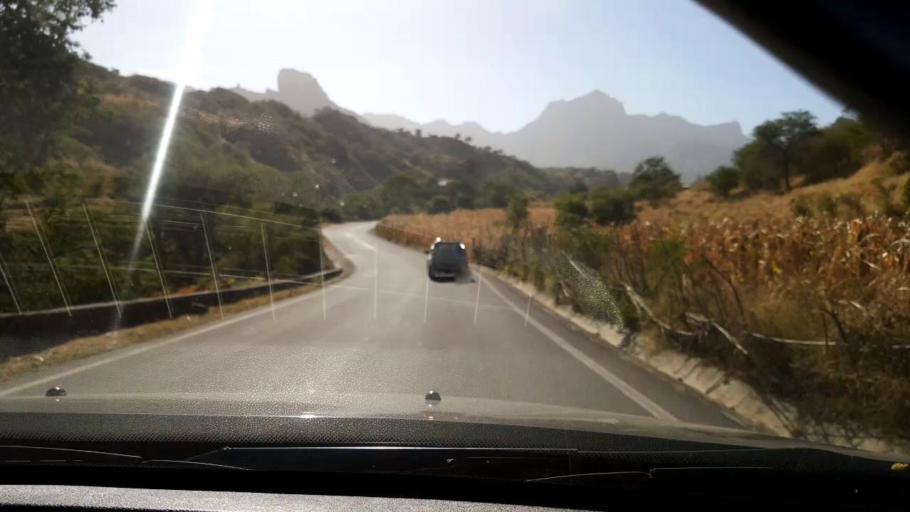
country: CV
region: Sao Lourenco dos Orgaos
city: Joao Teves
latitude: 15.0707
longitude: -23.5704
